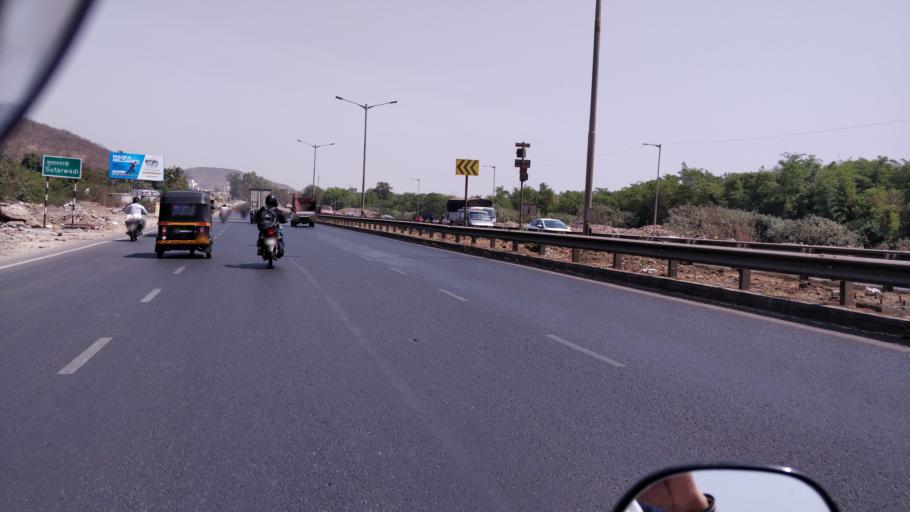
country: IN
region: Maharashtra
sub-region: Pune Division
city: Shivaji Nagar
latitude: 18.5299
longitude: 73.7788
